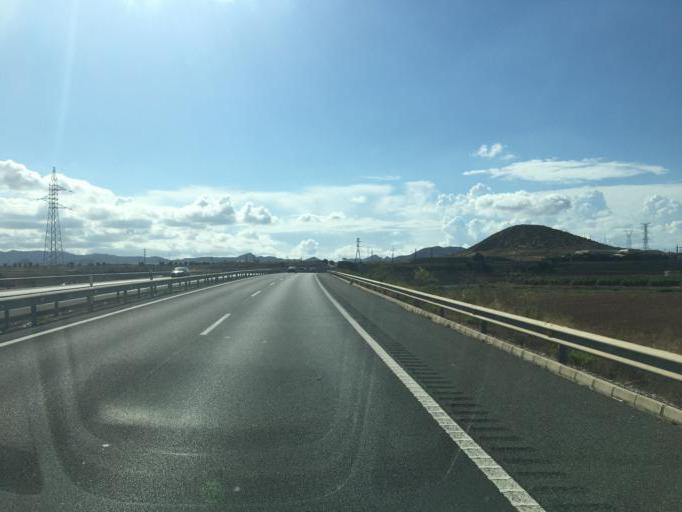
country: ES
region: Murcia
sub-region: Murcia
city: Cartagena
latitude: 37.6403
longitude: -0.9621
